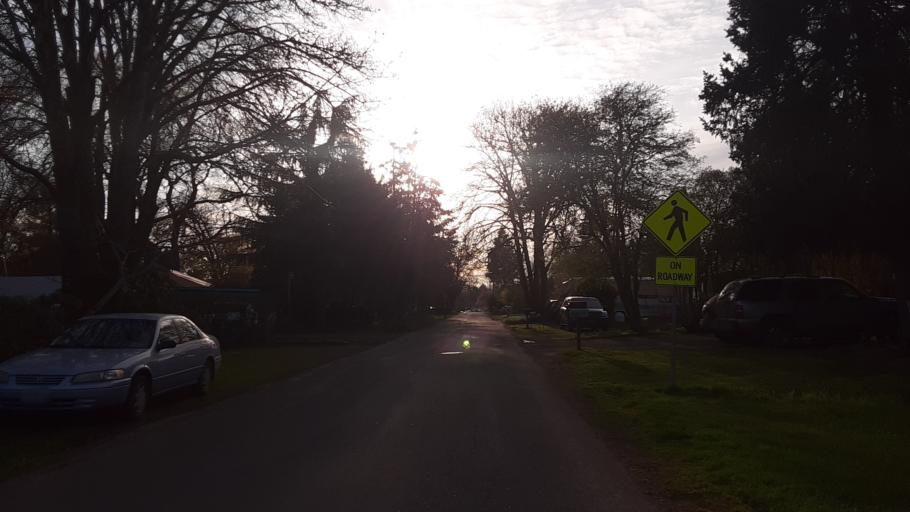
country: US
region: Oregon
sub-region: Benton County
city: Corvallis
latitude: 44.5494
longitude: -123.2589
